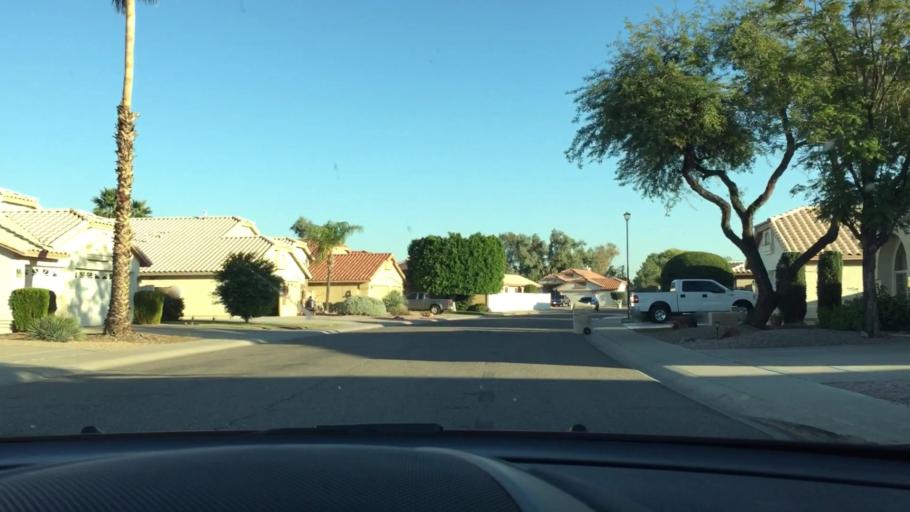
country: US
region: Arizona
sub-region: Maricopa County
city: Sun City
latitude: 33.6627
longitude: -112.2277
